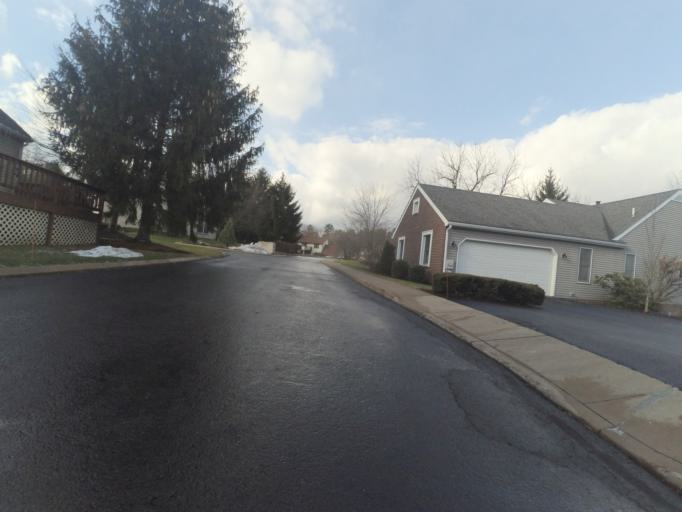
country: US
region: Pennsylvania
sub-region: Centre County
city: Lemont
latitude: 40.7915
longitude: -77.8332
